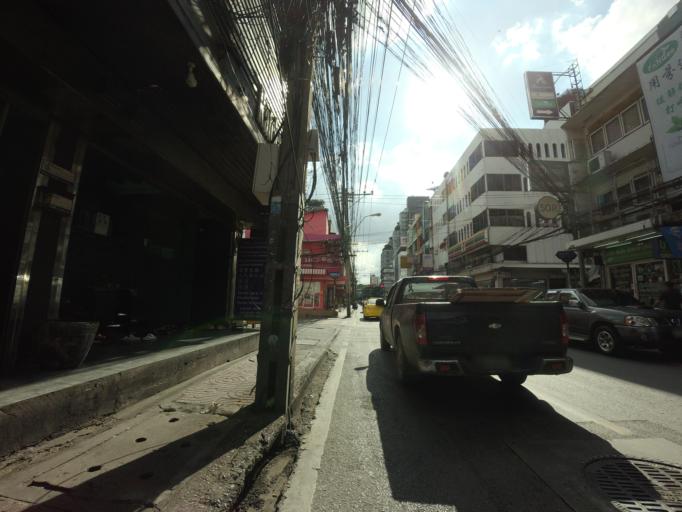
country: TH
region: Bangkok
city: Huai Khwang
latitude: 13.7786
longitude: 100.5764
